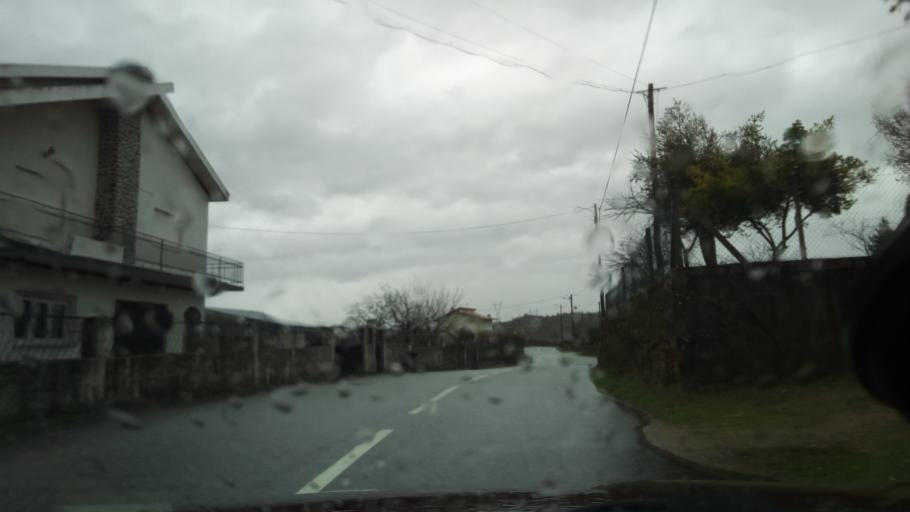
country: PT
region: Guarda
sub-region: Fornos de Algodres
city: Fornos de Algodres
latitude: 40.5697
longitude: -7.5121
